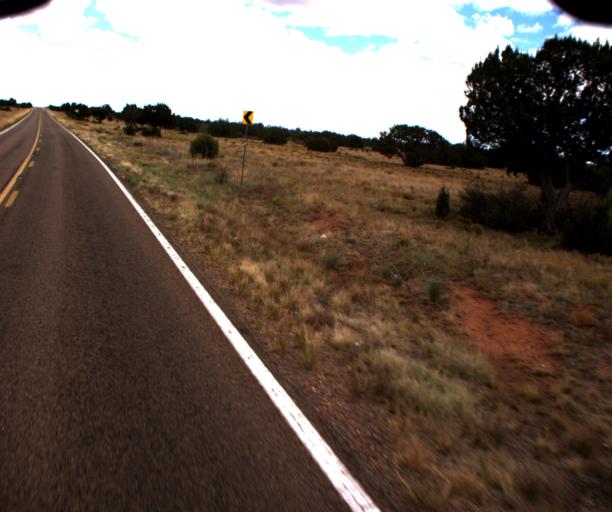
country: US
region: Arizona
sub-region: Navajo County
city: Heber-Overgaard
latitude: 34.5260
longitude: -110.4278
